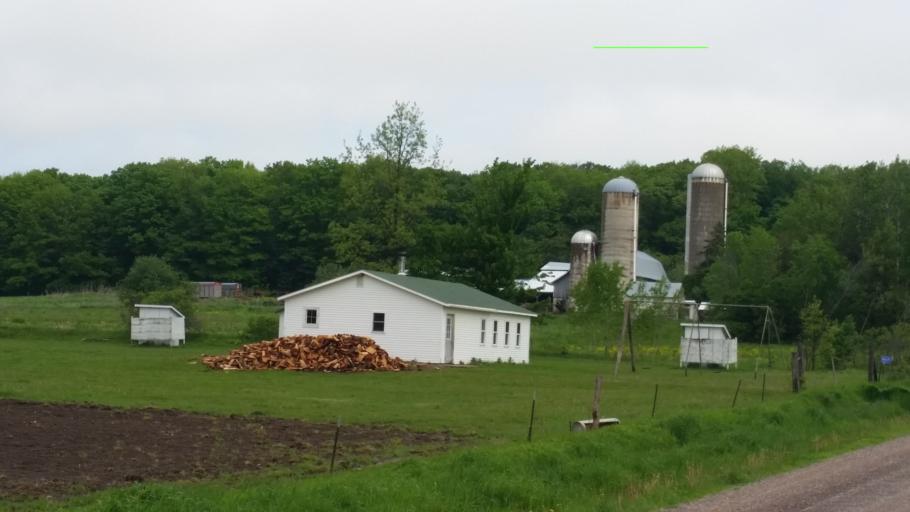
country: US
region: Wisconsin
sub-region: Clark County
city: Loyal
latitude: 44.6390
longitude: -90.4565
